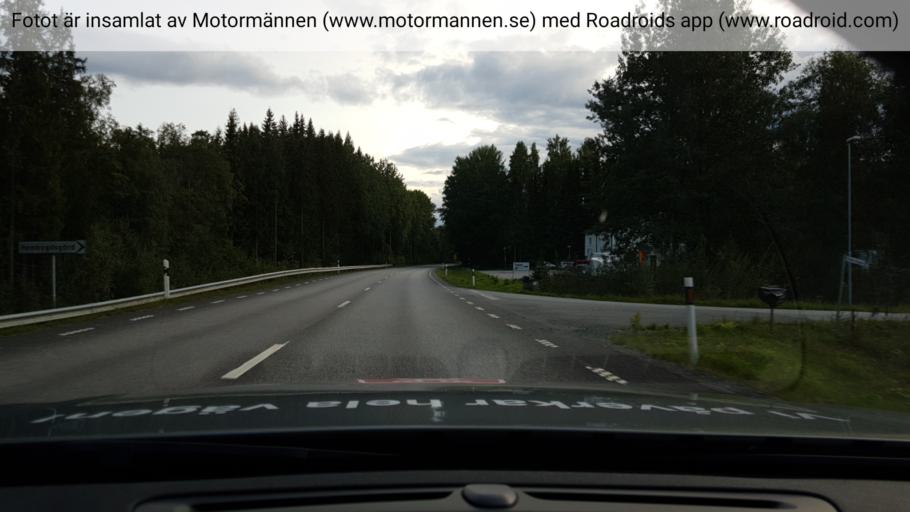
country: SE
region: OErebro
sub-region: Hallefors Kommun
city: Haellefors
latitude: 59.7919
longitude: 14.5430
